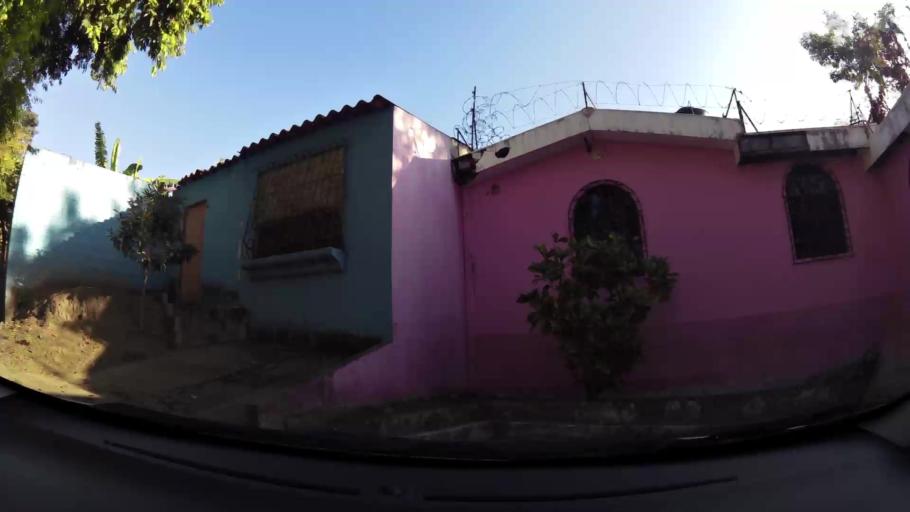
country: SV
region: La Libertad
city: Santa Tecla
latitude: 13.7422
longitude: -89.3526
